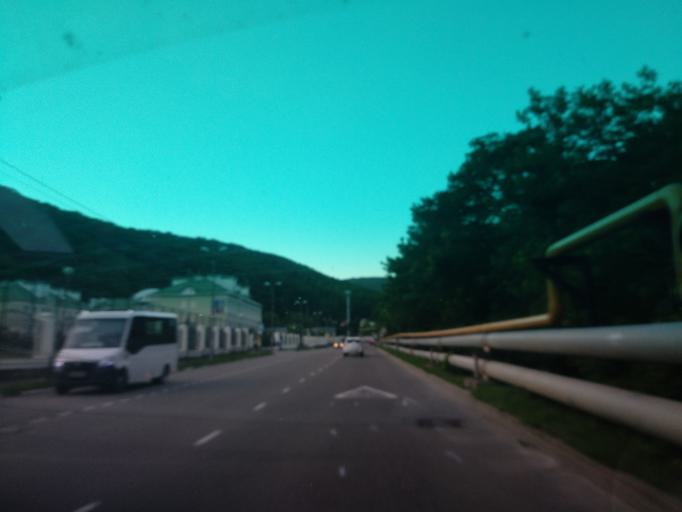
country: RU
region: Krasnodarskiy
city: Tuapse
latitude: 44.1191
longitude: 39.0695
